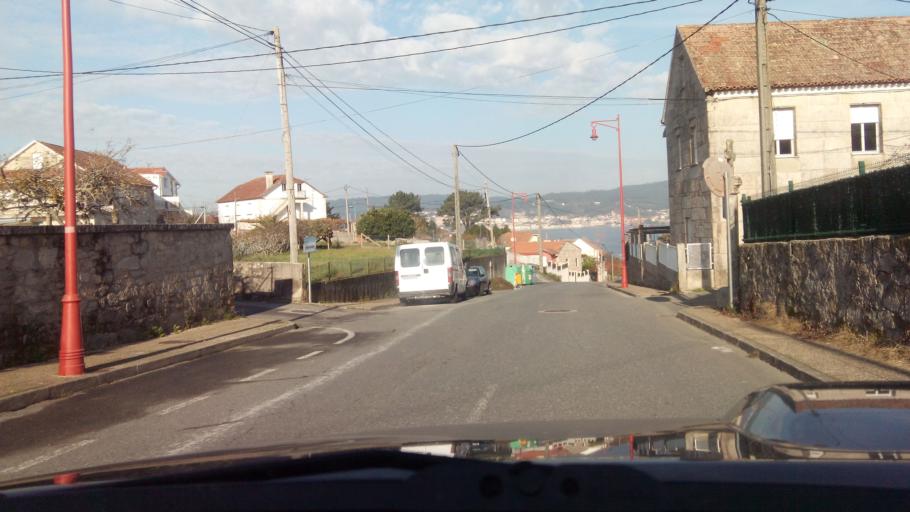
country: ES
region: Galicia
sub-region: Provincia de Pontevedra
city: Marin
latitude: 42.3707
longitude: -8.7358
